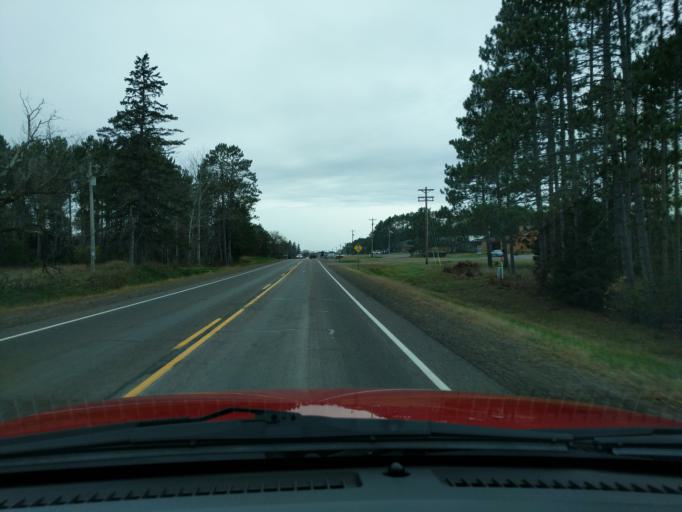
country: US
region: Wisconsin
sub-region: Washburn County
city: Spooner
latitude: 45.8219
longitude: -91.8787
